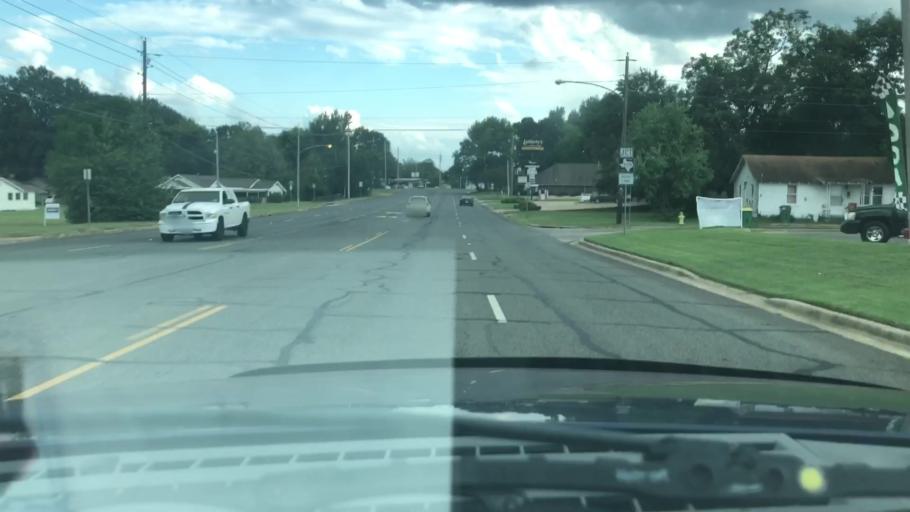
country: US
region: Texas
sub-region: Bowie County
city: Texarkana
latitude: 33.4449
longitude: -94.0650
